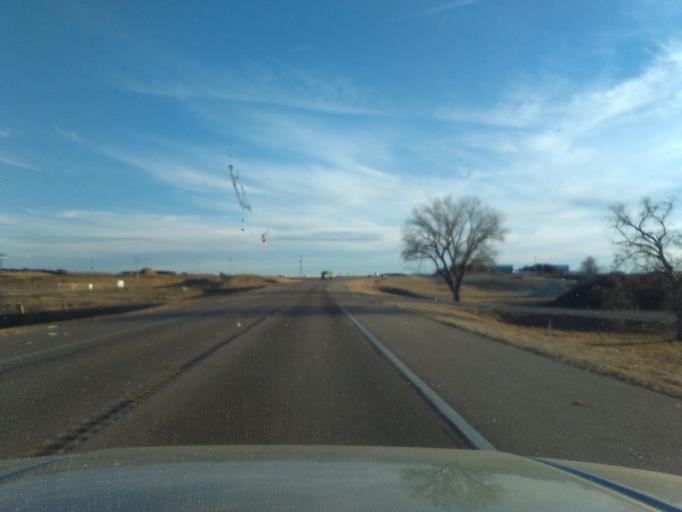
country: US
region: Kansas
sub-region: Logan County
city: Oakley
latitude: 39.1487
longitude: -100.8690
